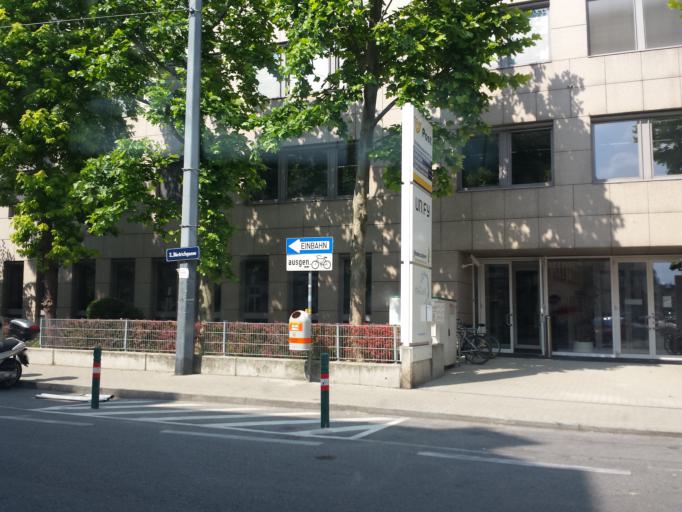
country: AT
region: Vienna
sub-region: Wien Stadt
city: Vienna
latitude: 48.1997
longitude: 16.4029
